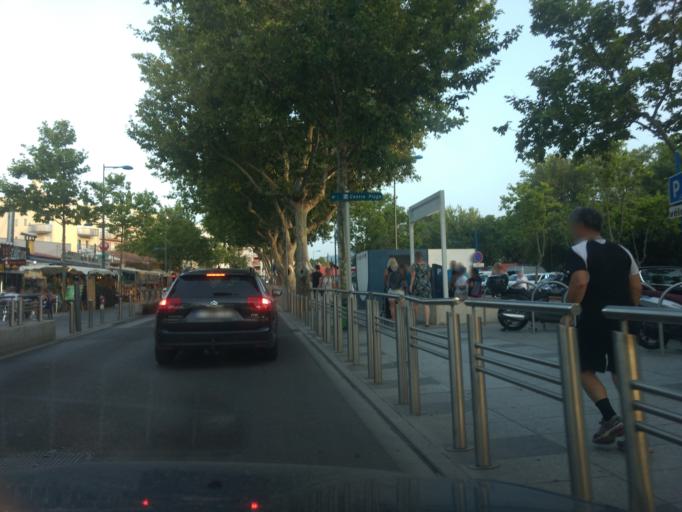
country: FR
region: Languedoc-Roussillon
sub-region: Departement des Pyrenees-Orientales
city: Argelers
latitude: 42.5522
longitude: 3.0458
